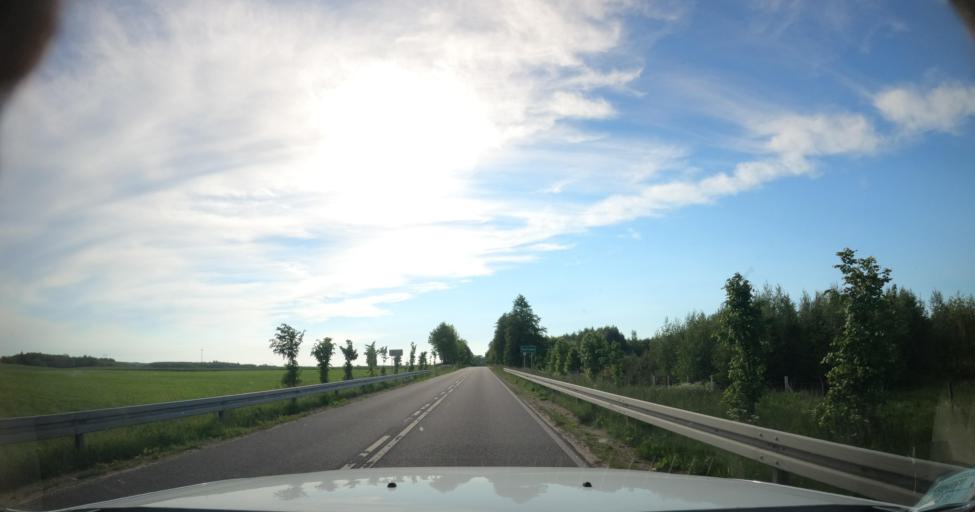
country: PL
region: Warmian-Masurian Voivodeship
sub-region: Powiat ostrodzki
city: Morag
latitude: 54.0818
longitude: 19.8938
